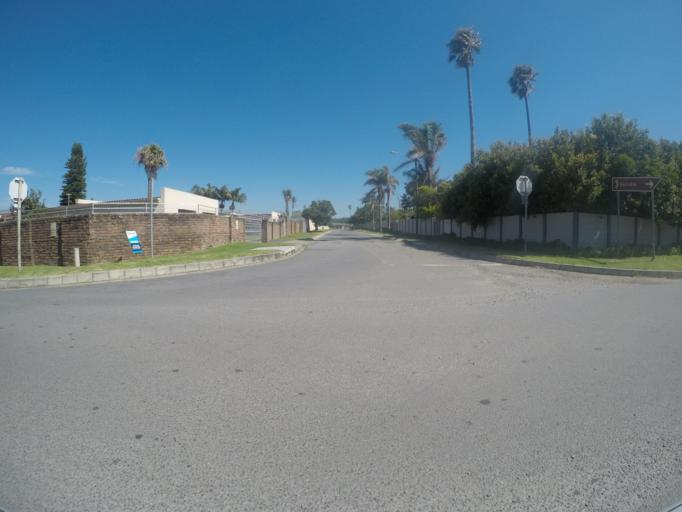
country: ZA
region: Eastern Cape
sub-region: Buffalo City Metropolitan Municipality
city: East London
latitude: -32.9483
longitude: 28.0040
